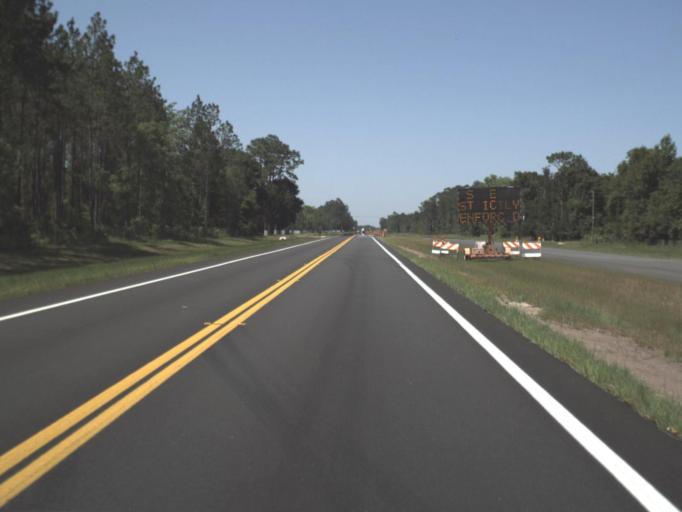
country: US
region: Florida
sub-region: Duval County
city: Baldwin
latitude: 30.3383
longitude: -81.9559
